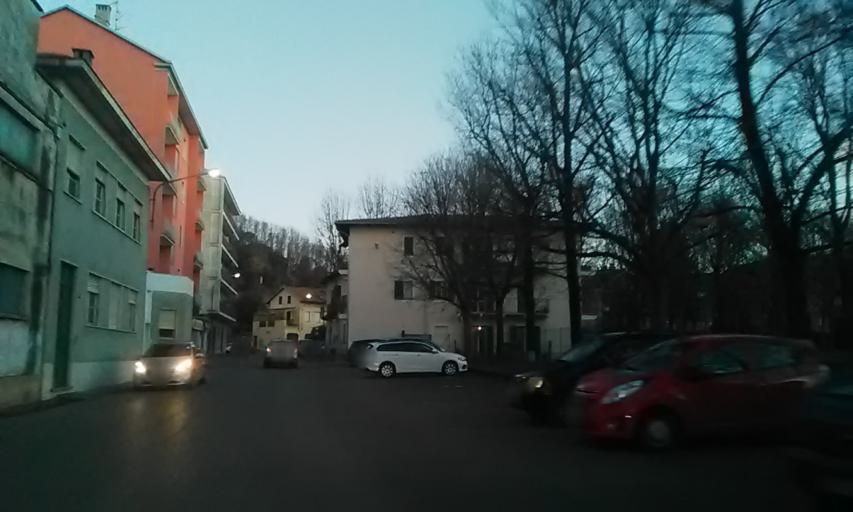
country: IT
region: Piedmont
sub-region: Provincia di Biella
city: Biella
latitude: 45.5572
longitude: 8.0410
